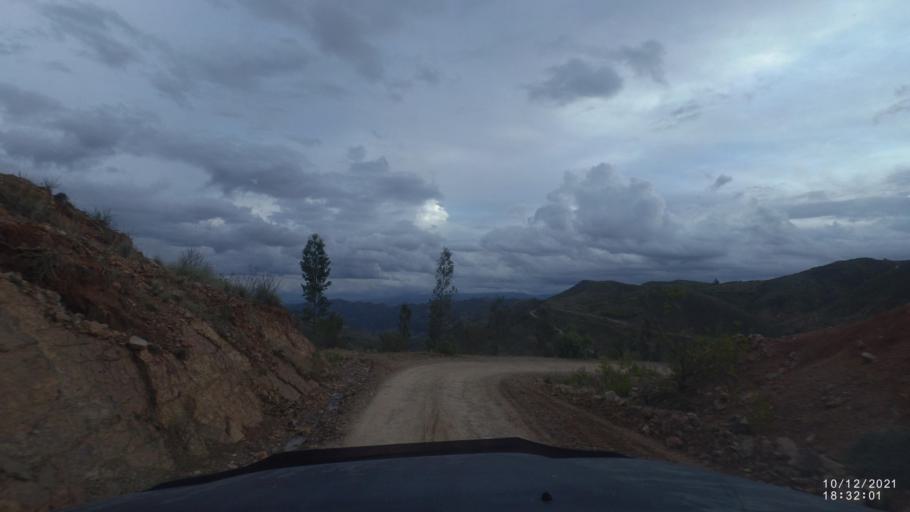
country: BO
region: Cochabamba
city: Tarata
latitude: -17.8165
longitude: -65.9862
